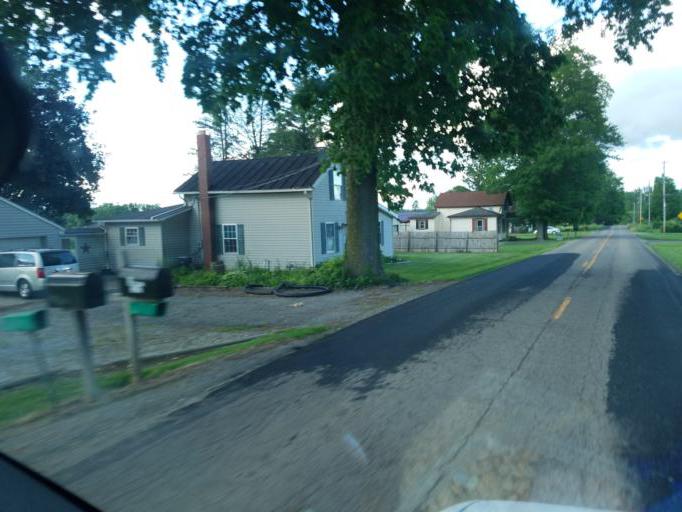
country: US
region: Ohio
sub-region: Knox County
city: Mount Vernon
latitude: 40.3893
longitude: -82.5104
